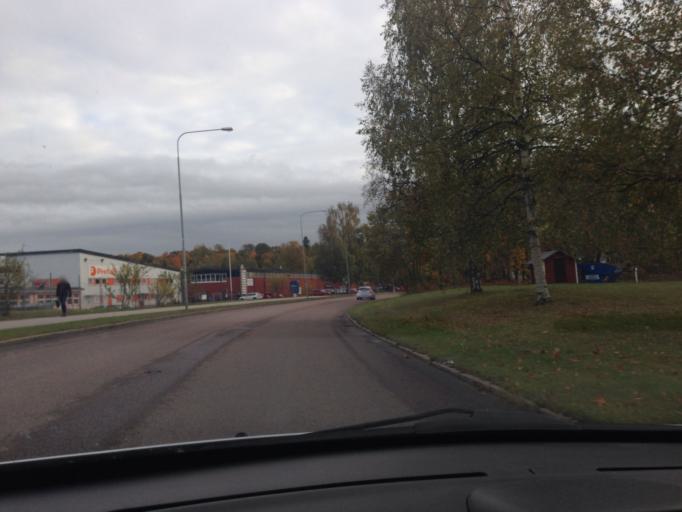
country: SE
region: Gaevleborg
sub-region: Gavle Kommun
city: Gavle
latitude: 60.6761
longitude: 17.1814
